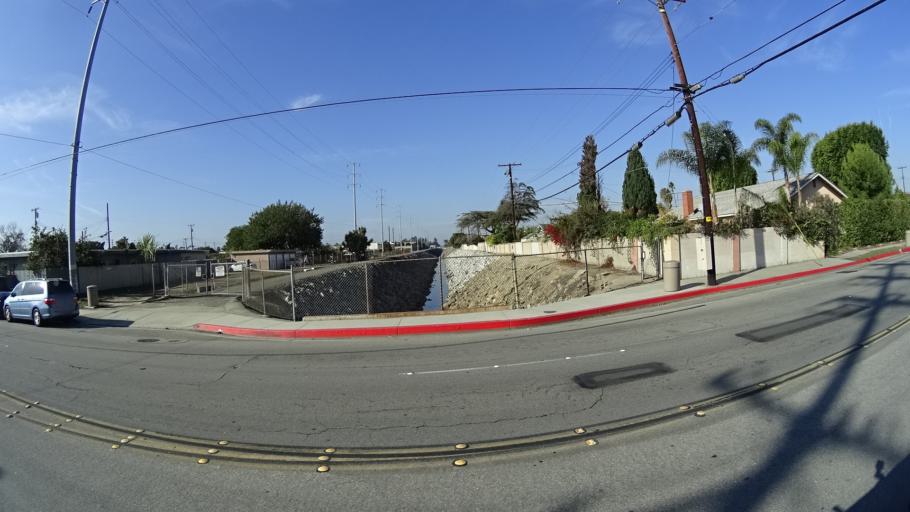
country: US
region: California
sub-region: Orange County
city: Fountain Valley
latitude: 33.7175
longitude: -117.9806
